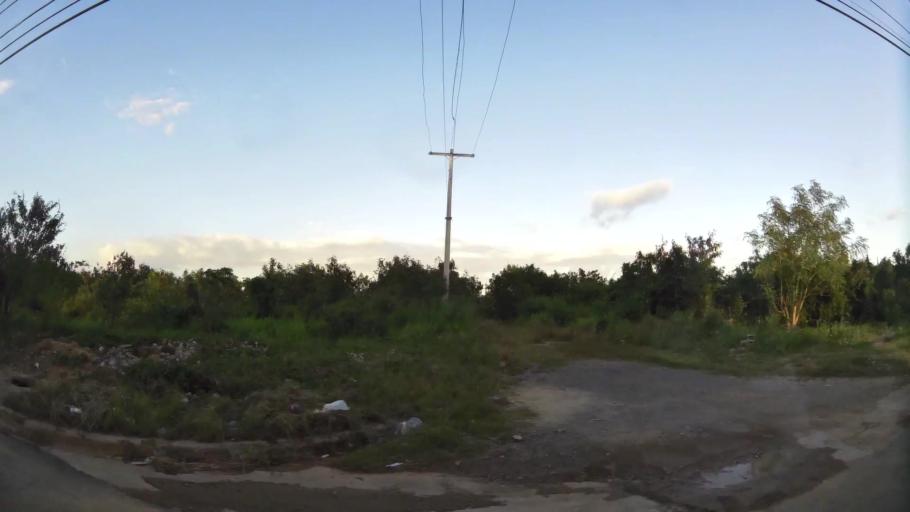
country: DO
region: Santo Domingo
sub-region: Santo Domingo
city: Santo Domingo Este
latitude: 18.4887
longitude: -69.8163
